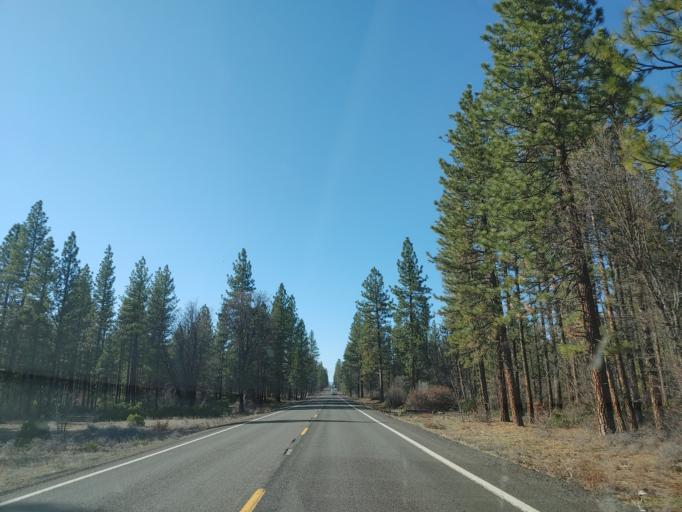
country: US
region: California
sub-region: Shasta County
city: Burney
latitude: 40.9241
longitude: -121.5981
